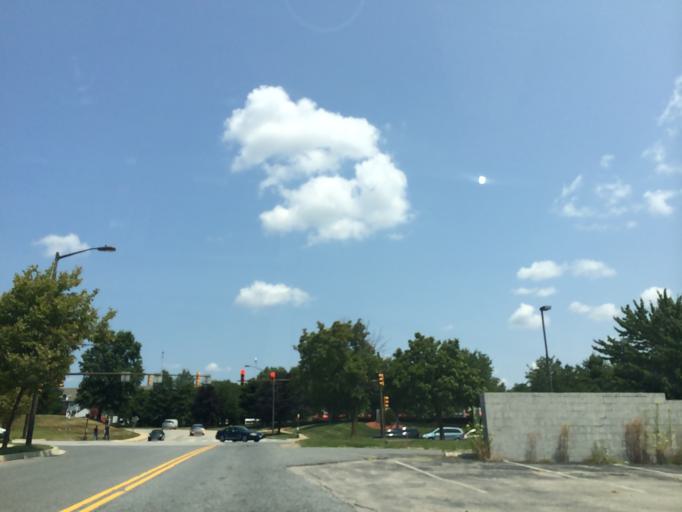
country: US
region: Maryland
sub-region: Howard County
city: Riverside
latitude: 39.1762
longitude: -76.8450
